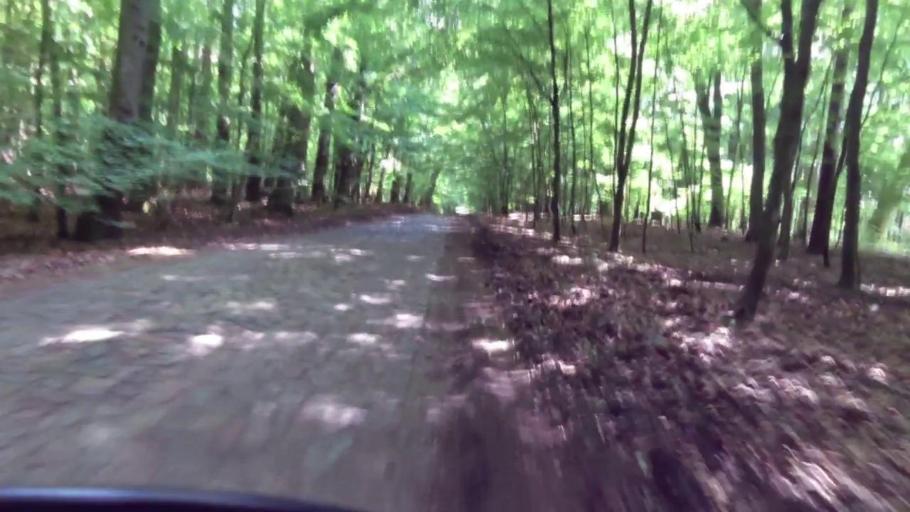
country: PL
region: West Pomeranian Voivodeship
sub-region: Powiat kamienski
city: Miedzyzdroje
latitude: 53.8820
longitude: 14.4816
